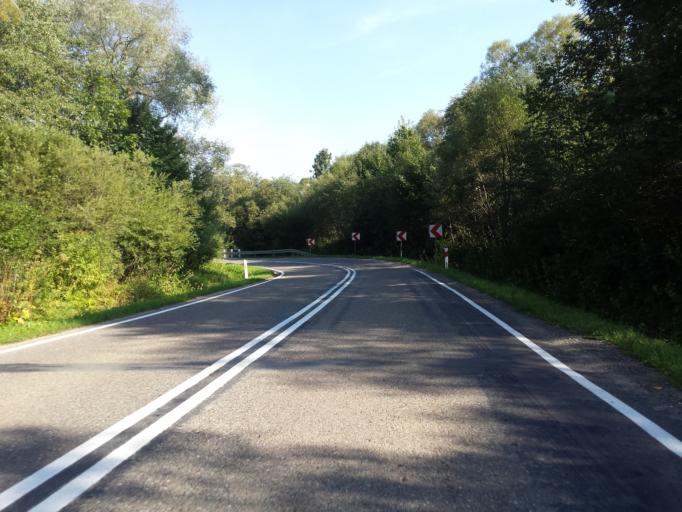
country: PL
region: Subcarpathian Voivodeship
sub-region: Powiat leski
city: Baligrod
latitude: 49.2652
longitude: 22.2871
